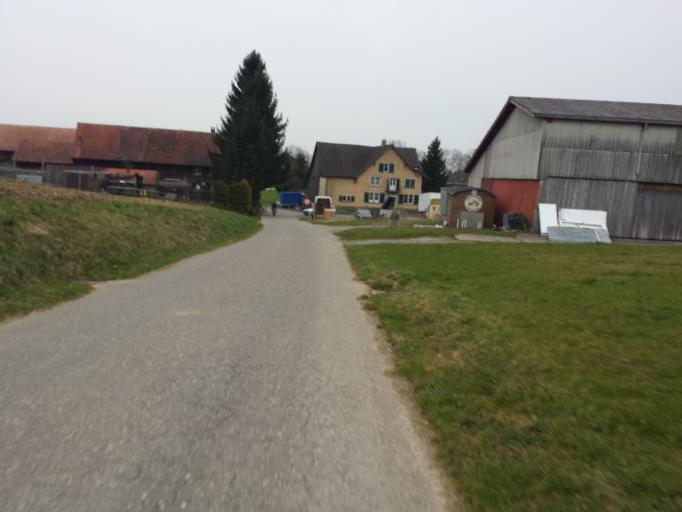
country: CH
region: Thurgau
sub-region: Arbon District
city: Salmsach
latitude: 47.5518
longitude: 9.3553
